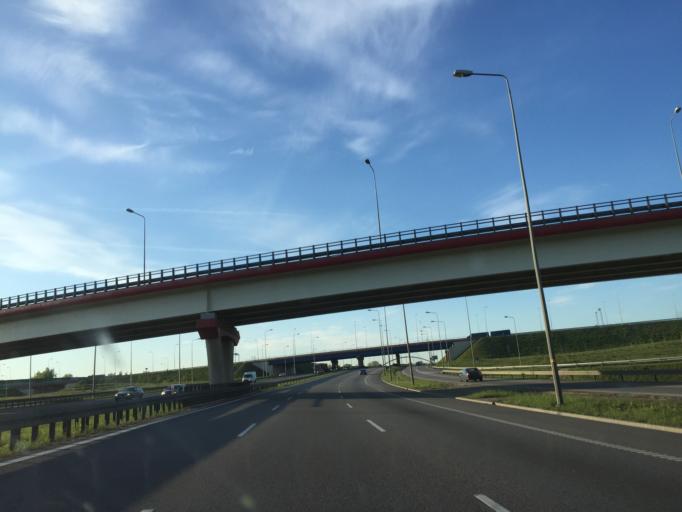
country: PL
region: Pomeranian Voivodeship
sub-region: Powiat gdanski
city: Kowale
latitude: 54.3468
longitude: 18.5193
